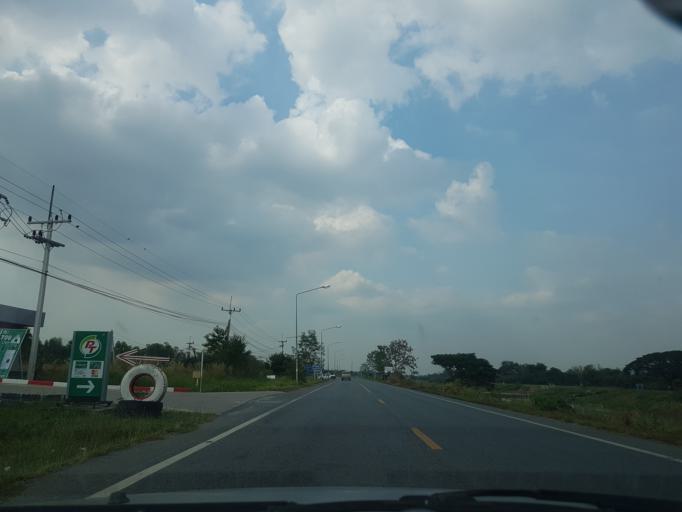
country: TH
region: Phra Nakhon Si Ayutthaya
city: Phachi
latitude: 14.4772
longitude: 100.7437
